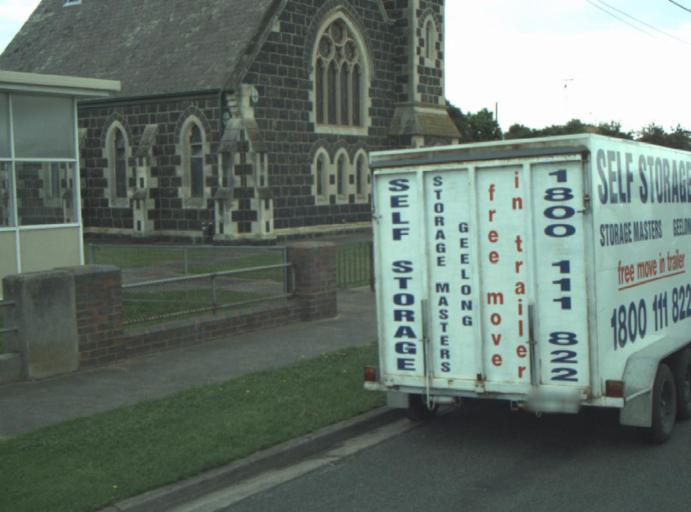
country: AU
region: Victoria
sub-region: Greater Geelong
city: Breakwater
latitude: -38.1842
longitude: 144.3889
